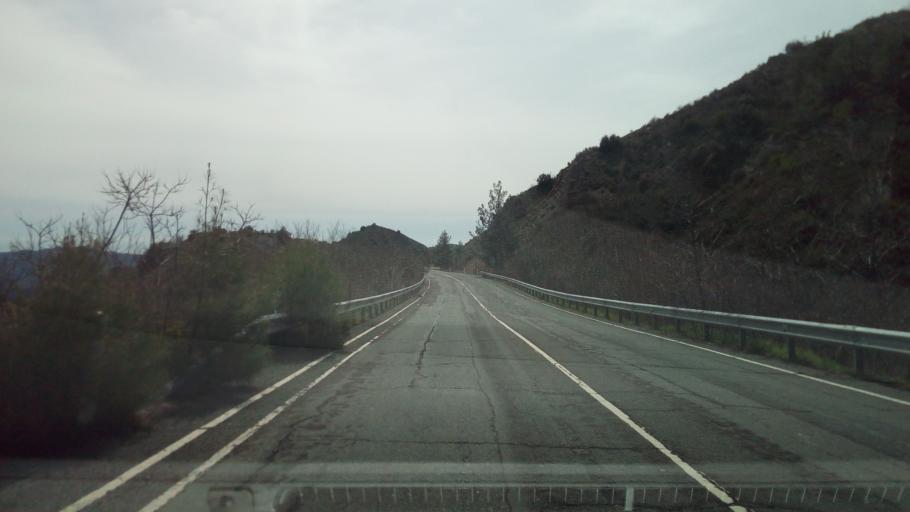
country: CY
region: Limassol
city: Pelendri
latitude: 34.8783
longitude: 32.9450
